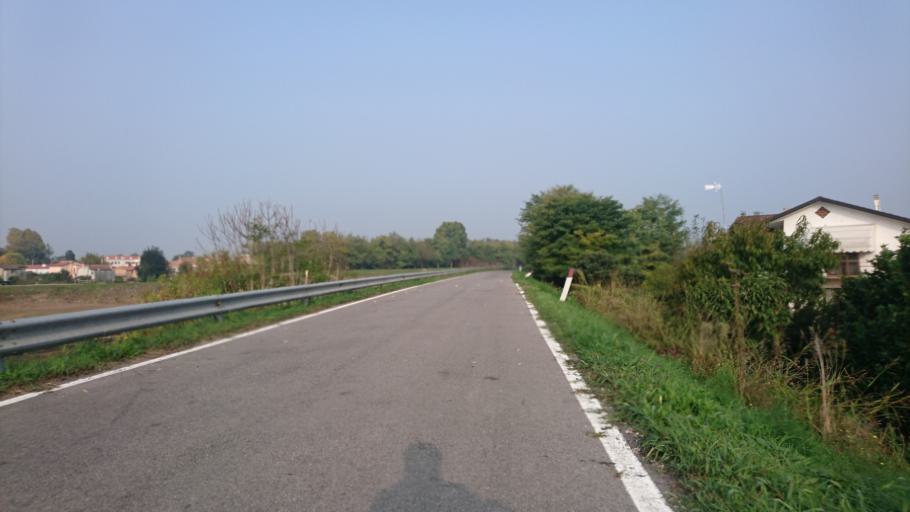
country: IT
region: Veneto
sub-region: Provincia di Padova
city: Limena
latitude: 45.4807
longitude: 11.8482
